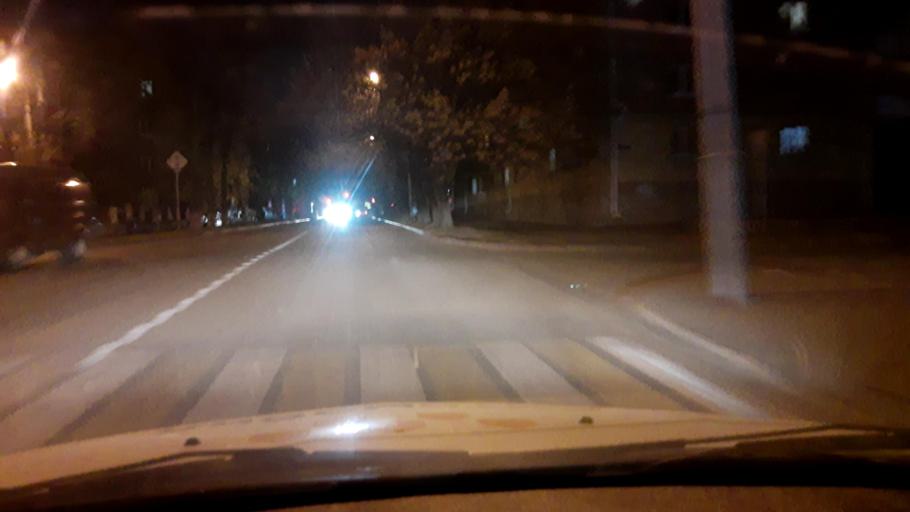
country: RU
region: Bashkortostan
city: Ufa
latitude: 54.8192
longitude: 56.0796
